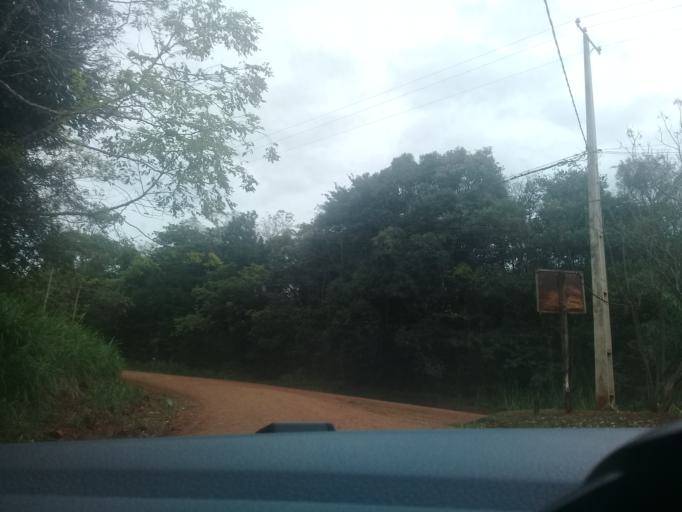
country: AR
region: Misiones
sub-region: Departamento de Obera
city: Obera
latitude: -27.4797
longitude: -55.1531
